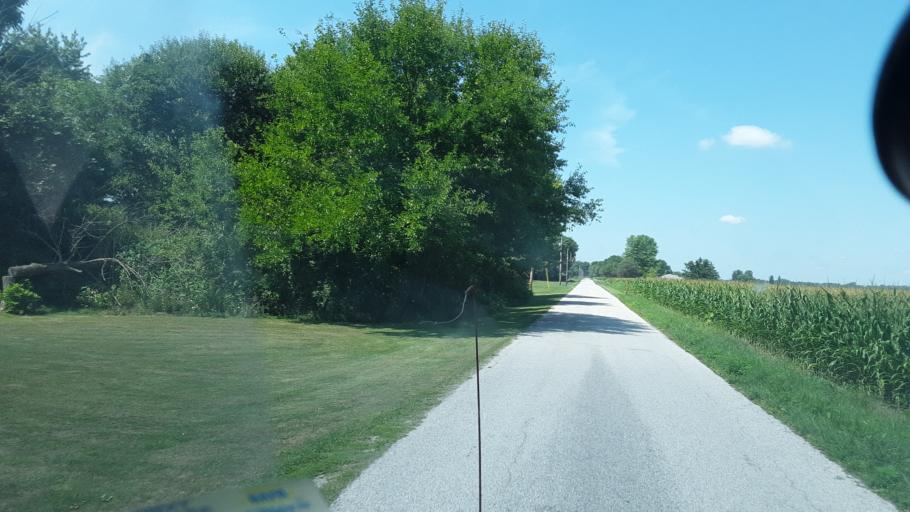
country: US
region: Ohio
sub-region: Hancock County
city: Findlay
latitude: 40.9922
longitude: -83.5231
